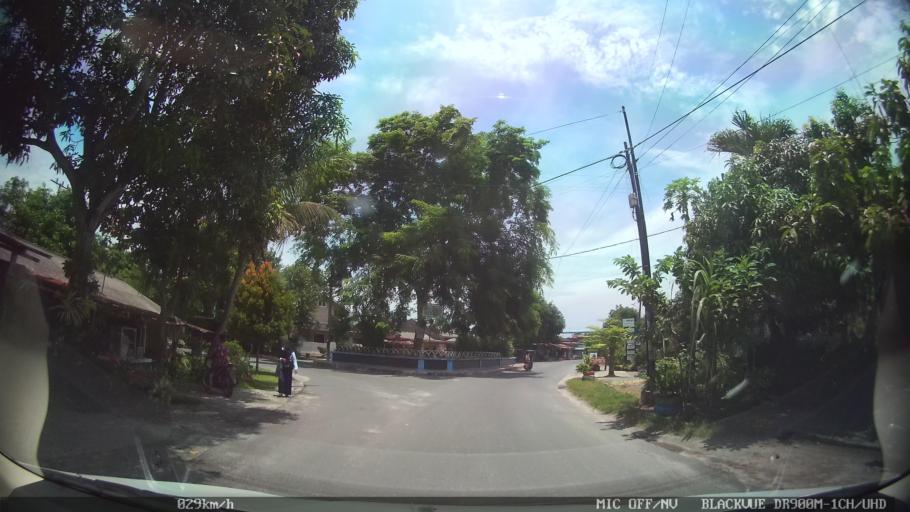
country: ID
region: North Sumatra
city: Percut
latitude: 3.5424
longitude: 98.8759
